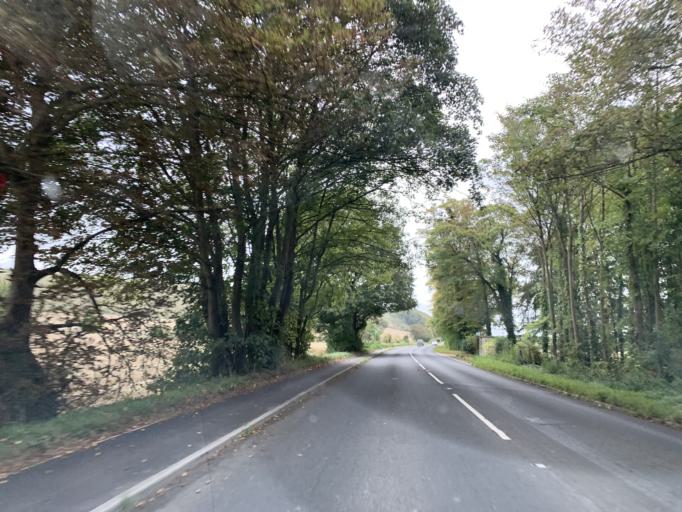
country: GB
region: England
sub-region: Wiltshire
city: Bishopstrow
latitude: 51.1916
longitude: -2.1302
